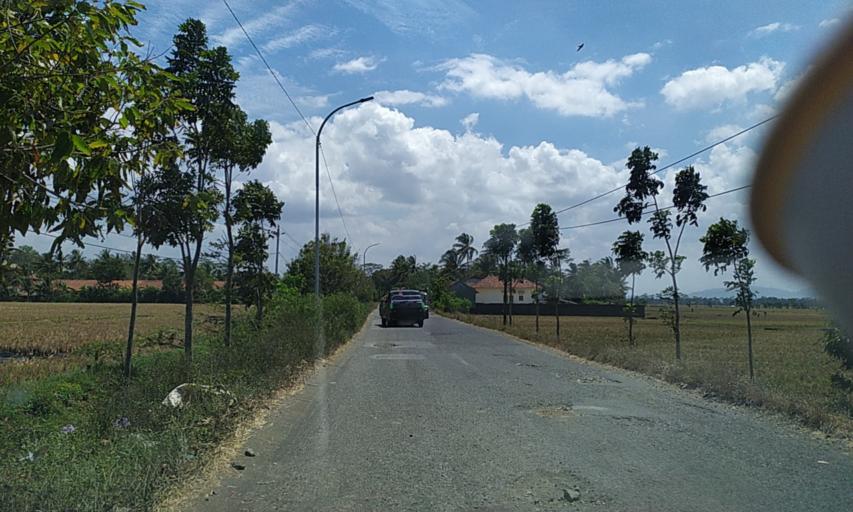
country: ID
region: Central Java
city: Adipala
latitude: -7.6520
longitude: 109.1519
